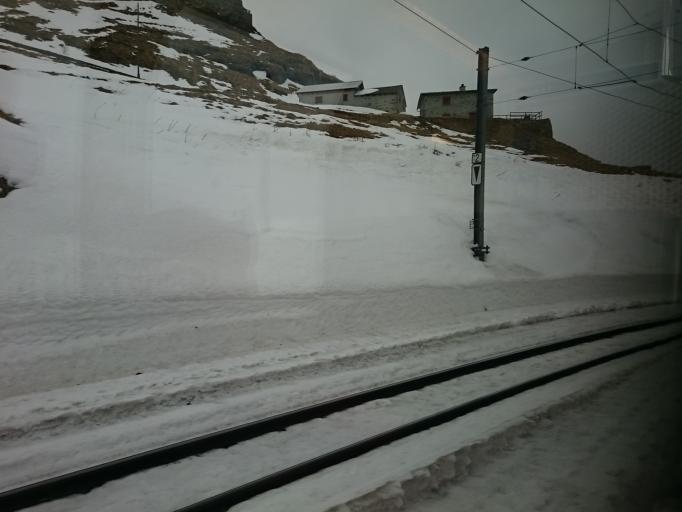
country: CH
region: Grisons
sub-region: Bernina District
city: Poschiavo
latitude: 46.3739
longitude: 10.0325
